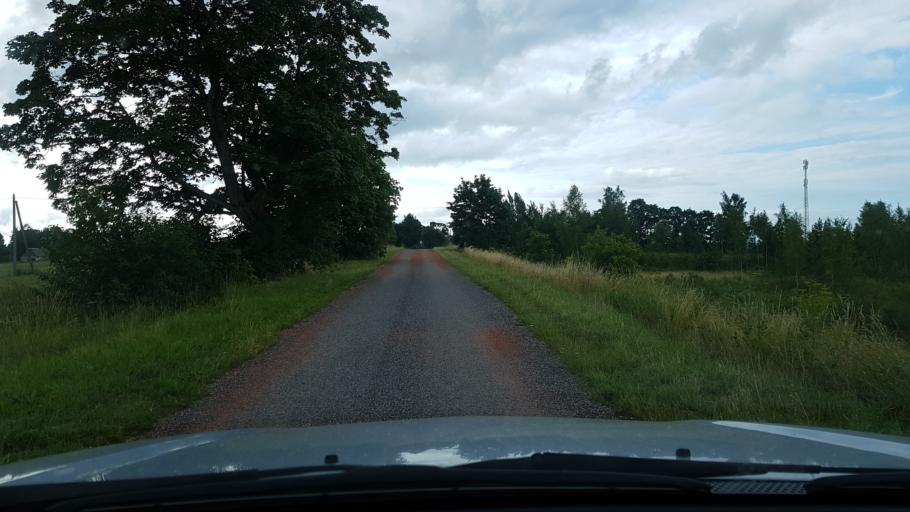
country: EE
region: Ida-Virumaa
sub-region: Narva-Joesuu linn
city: Narva-Joesuu
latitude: 59.3930
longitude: 27.9742
